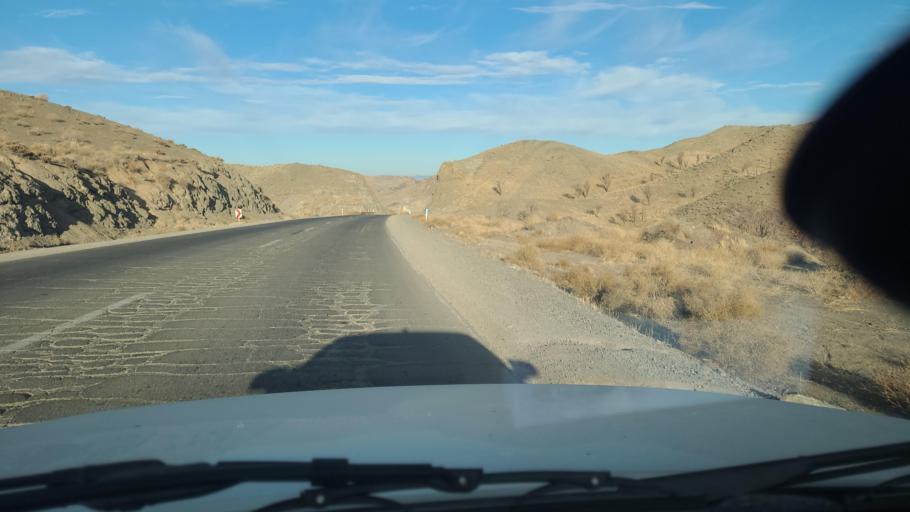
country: IR
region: Razavi Khorasan
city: Sabzevar
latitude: 36.4165
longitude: 57.5530
